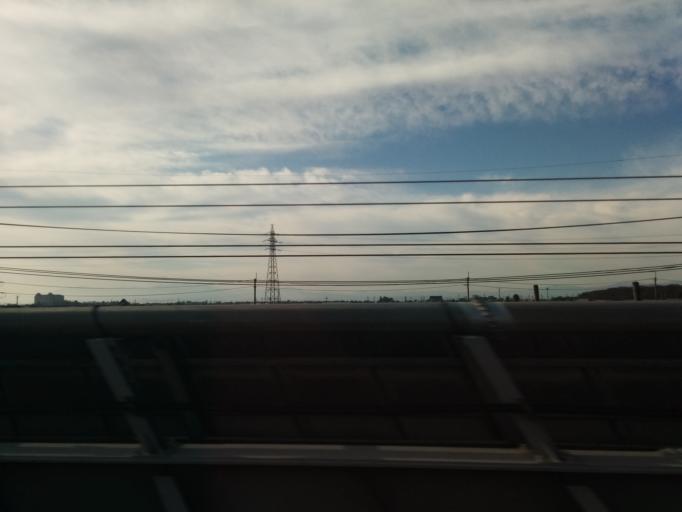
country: JP
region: Shiga Prefecture
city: Nagahama
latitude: 35.3240
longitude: 136.2917
